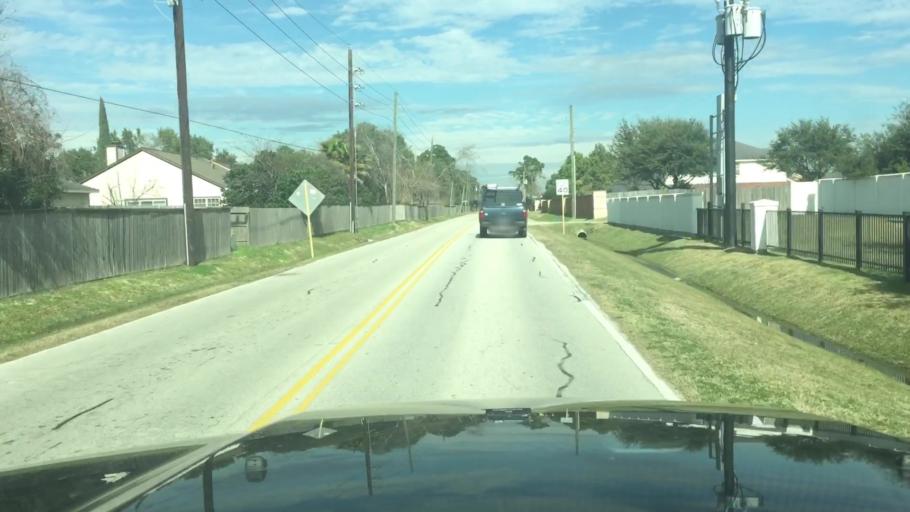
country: US
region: Texas
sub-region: Harris County
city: Oak Cliff Place
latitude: 29.8317
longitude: -95.6751
